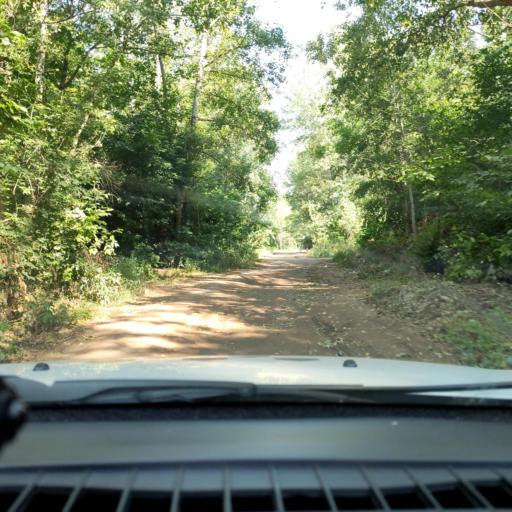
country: RU
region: Samara
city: Smyshlyayevka
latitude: 53.2052
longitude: 50.3293
